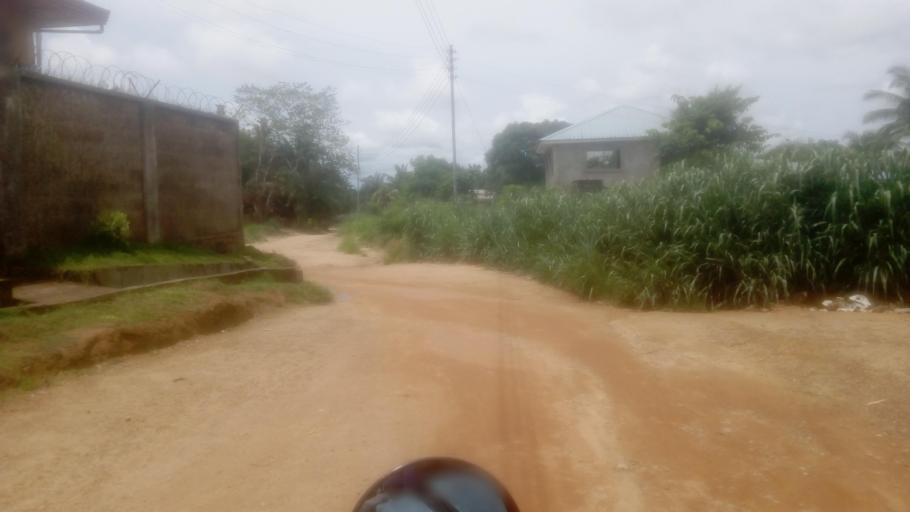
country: SL
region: Southern Province
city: Bo
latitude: 7.9510
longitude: -11.7148
